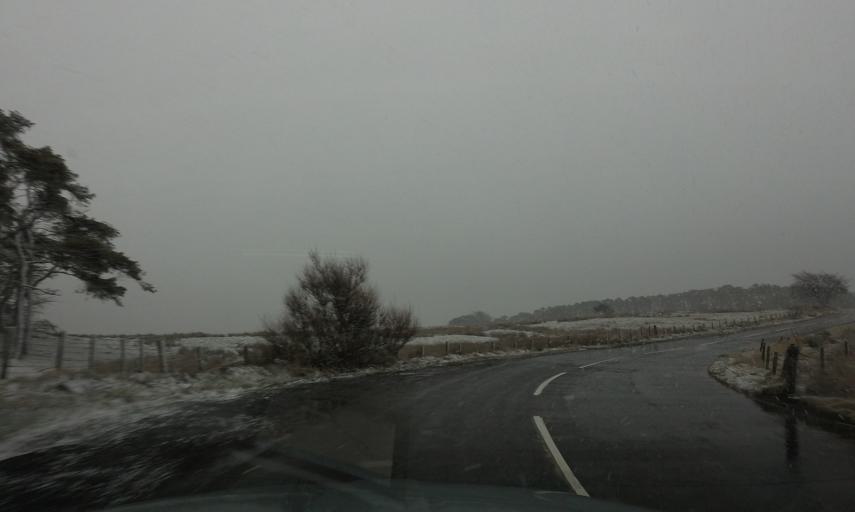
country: GB
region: Scotland
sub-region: North Lanarkshire
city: Shotts
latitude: 55.8385
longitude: -3.8378
